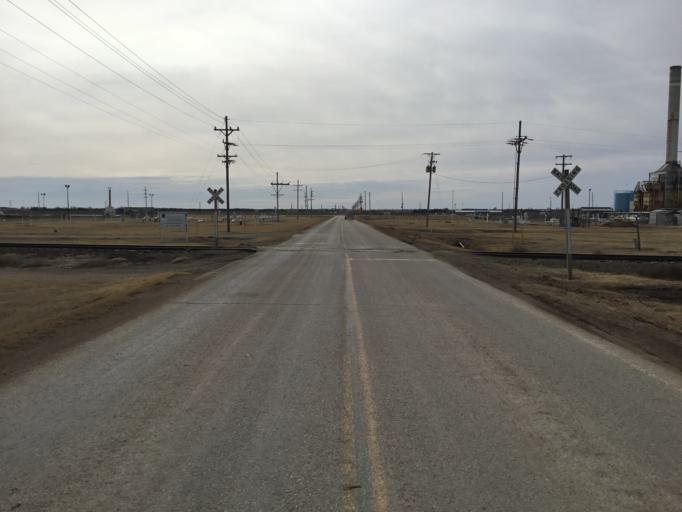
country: US
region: Kansas
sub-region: McPherson County
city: Inman
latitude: 38.3801
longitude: -97.8324
